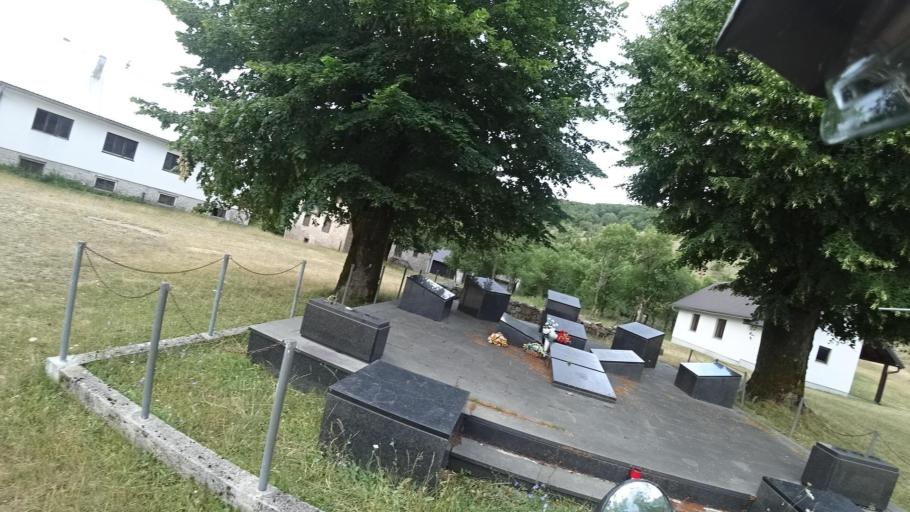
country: HR
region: Licko-Senjska
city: Jezerce
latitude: 44.7353
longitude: 15.4894
